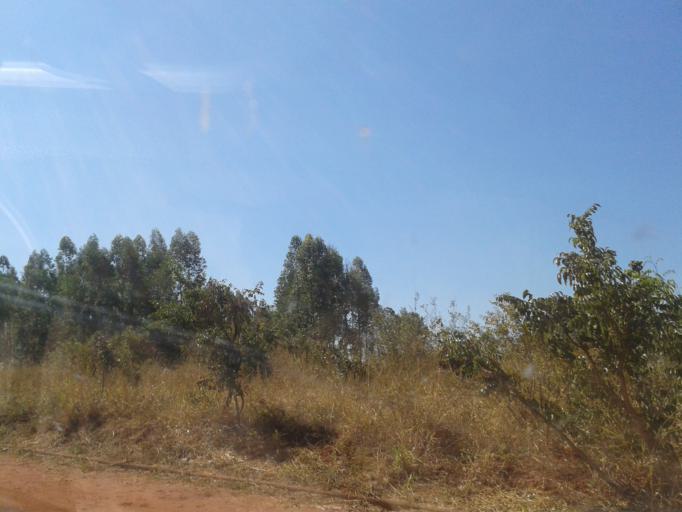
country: BR
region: Minas Gerais
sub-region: Ituiutaba
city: Ituiutaba
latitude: -19.0045
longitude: -49.4756
